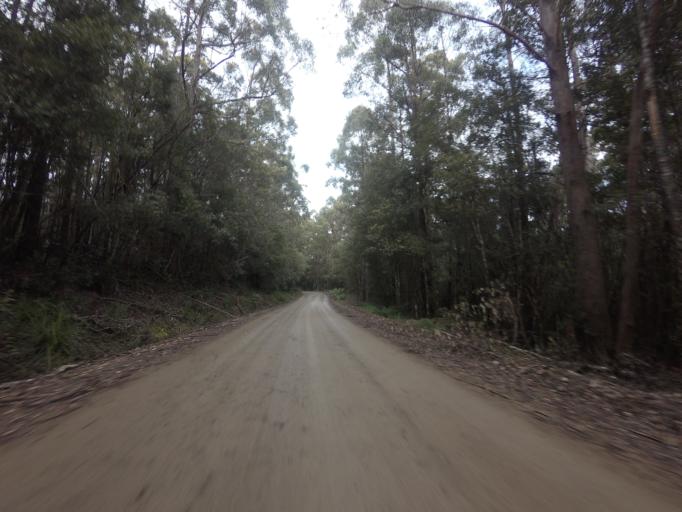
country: AU
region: Tasmania
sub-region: Huon Valley
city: Geeveston
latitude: -43.4940
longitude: 146.8809
